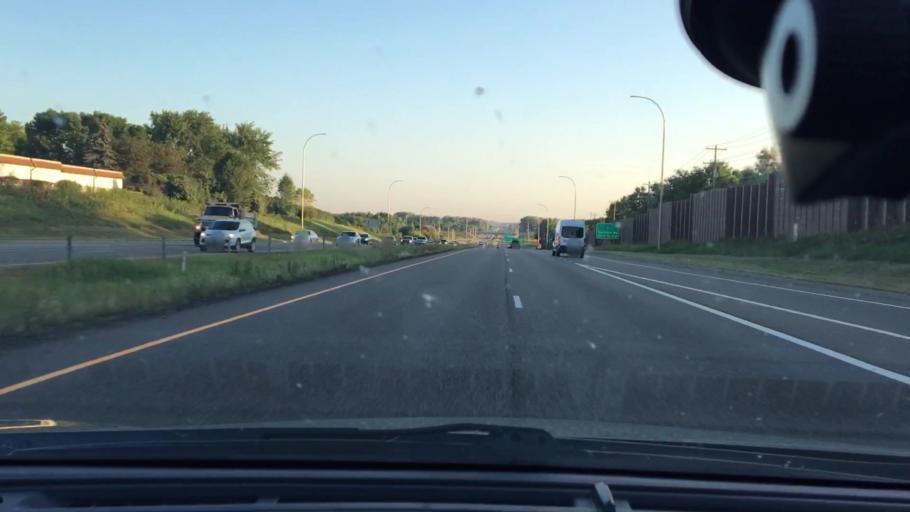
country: US
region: Minnesota
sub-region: Hennepin County
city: New Hope
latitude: 45.0245
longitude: -93.4000
